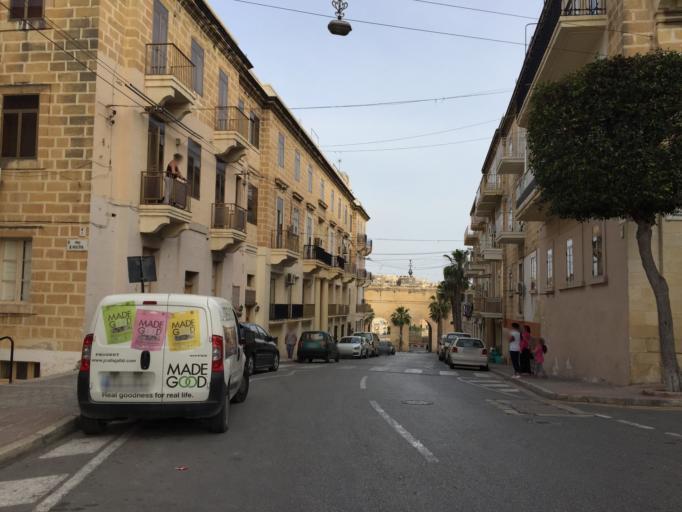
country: MT
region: L-Isla
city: Senglea
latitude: 35.8857
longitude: 14.5185
